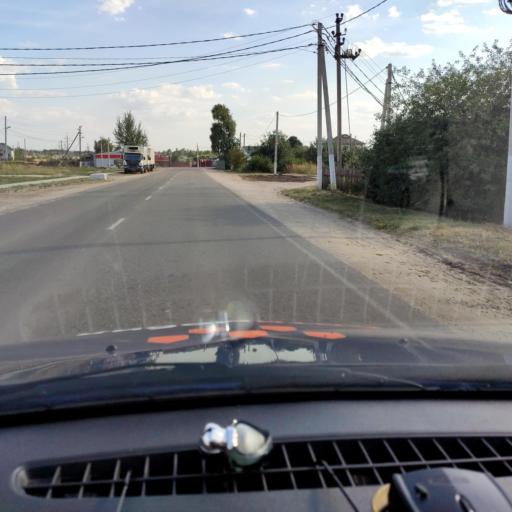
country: RU
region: Voronezj
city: Podgornoye
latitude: 51.8896
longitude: 39.1765
